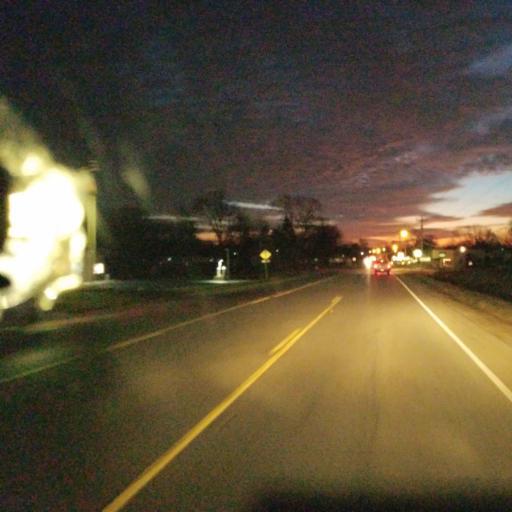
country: US
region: Illinois
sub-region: Peoria County
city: Hanna City
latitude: 40.6930
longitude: -89.8014
